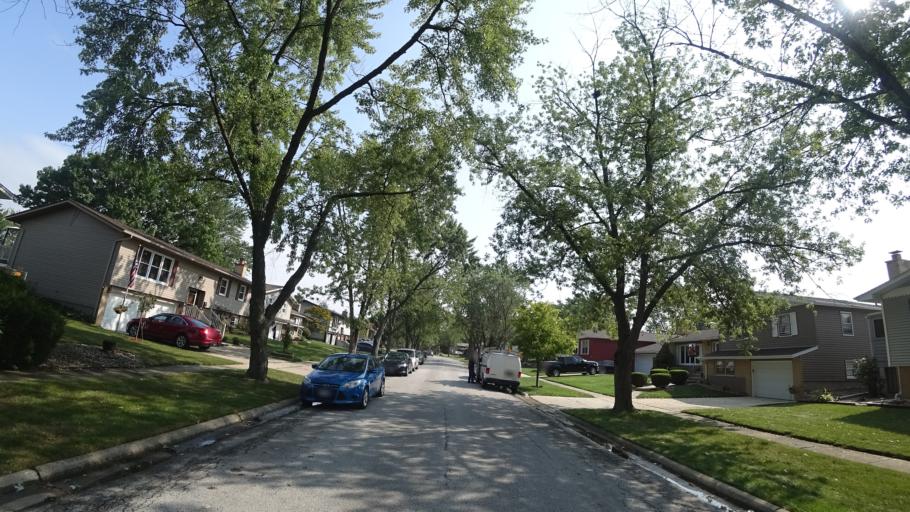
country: US
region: Illinois
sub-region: Cook County
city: Oak Forest
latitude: 41.6144
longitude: -87.7704
